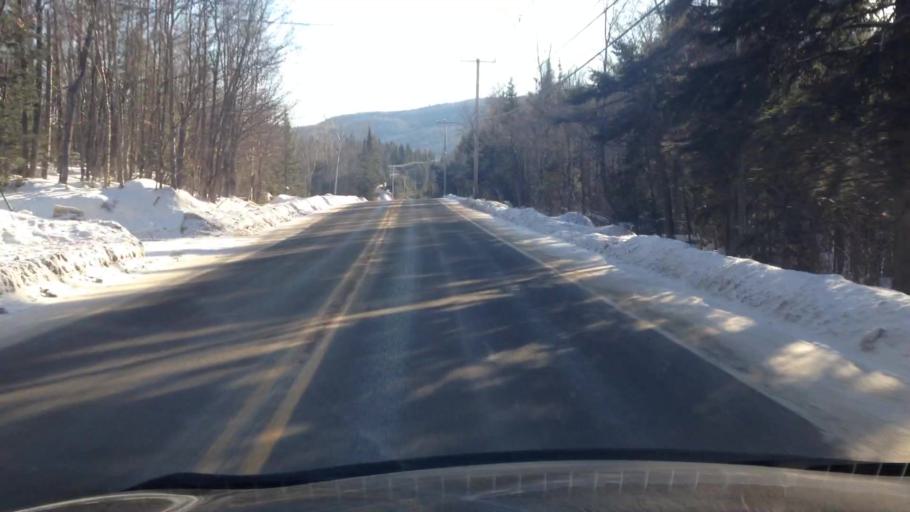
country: CA
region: Quebec
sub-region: Laurentides
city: Sainte-Agathe-des-Monts
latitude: 45.9088
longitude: -74.3315
